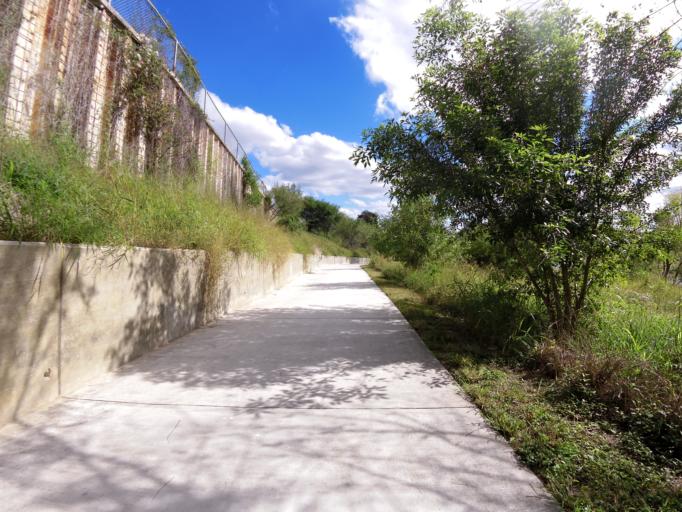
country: US
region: Texas
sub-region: Bexar County
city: San Antonio
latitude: 29.3917
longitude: -98.4992
